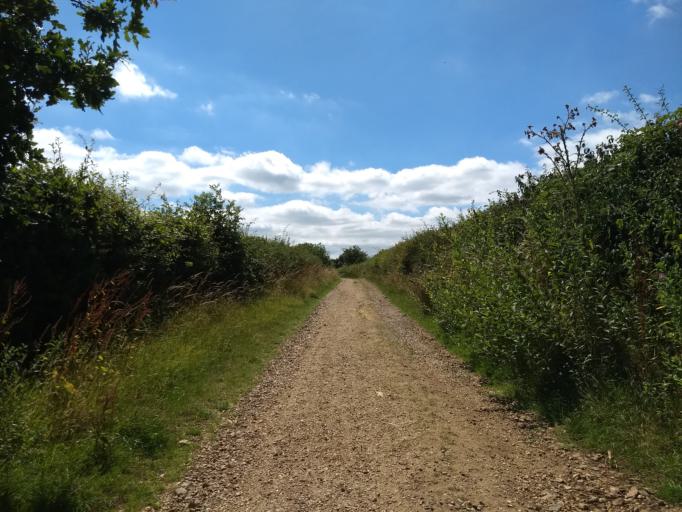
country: GB
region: England
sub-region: Isle of Wight
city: Brading
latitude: 50.7070
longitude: -1.1399
